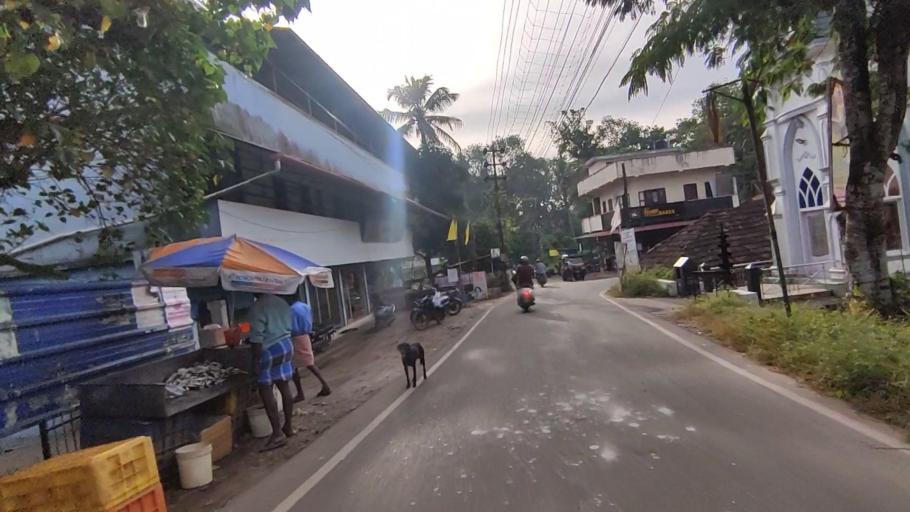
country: IN
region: Kerala
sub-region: Kottayam
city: Kottayam
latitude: 9.6010
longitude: 76.4926
